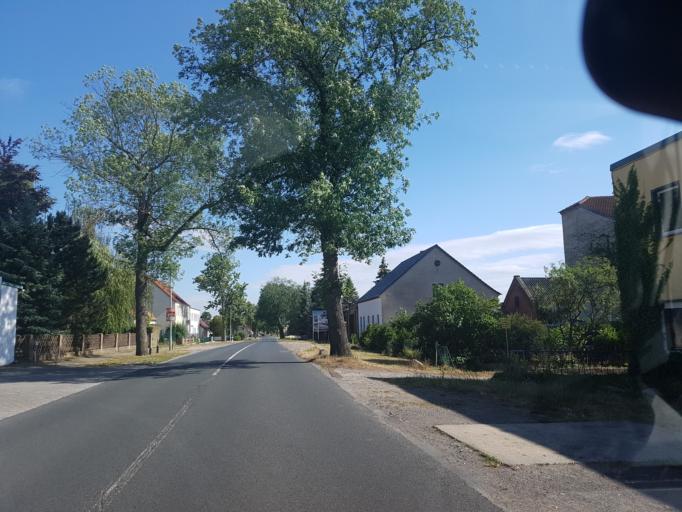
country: DE
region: Brandenburg
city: Juterbog
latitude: 51.9814
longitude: 13.1008
